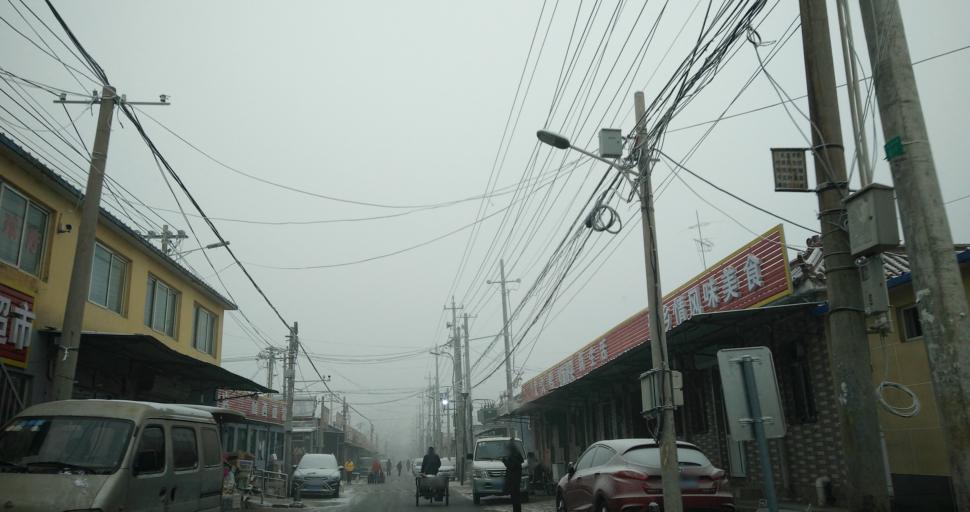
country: CN
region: Beijing
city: Yinghai
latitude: 39.7183
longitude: 116.4272
